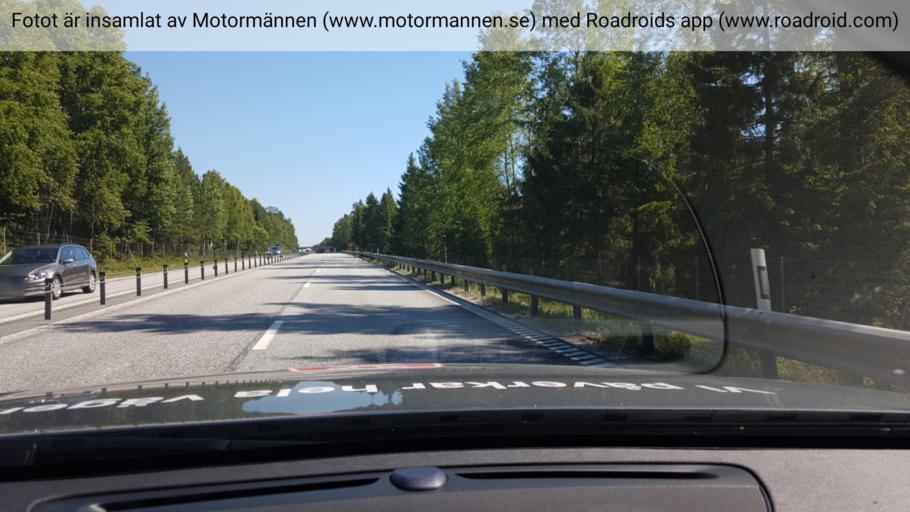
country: SE
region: Stockholm
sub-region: Osterakers Kommun
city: Akersberga
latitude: 59.5340
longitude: 18.1997
